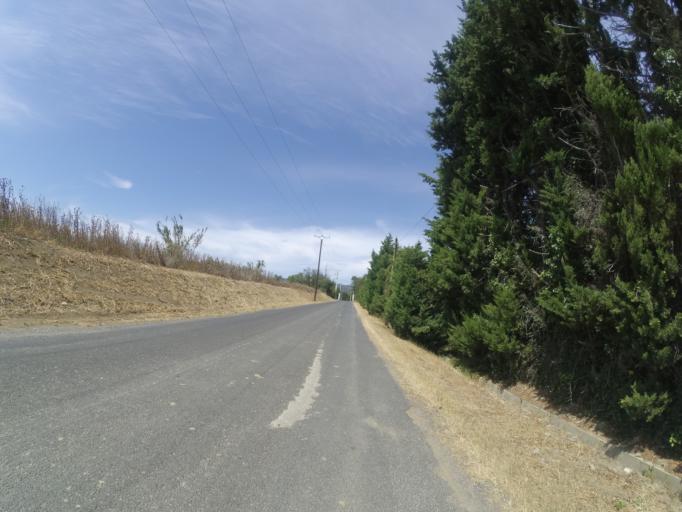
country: FR
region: Languedoc-Roussillon
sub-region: Departement des Pyrenees-Orientales
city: Millas
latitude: 42.6797
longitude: 2.6687
